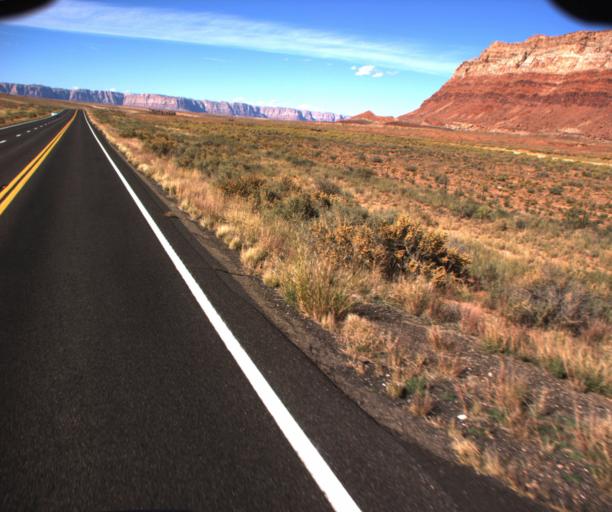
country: US
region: Arizona
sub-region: Coconino County
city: LeChee
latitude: 36.5826
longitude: -111.6481
